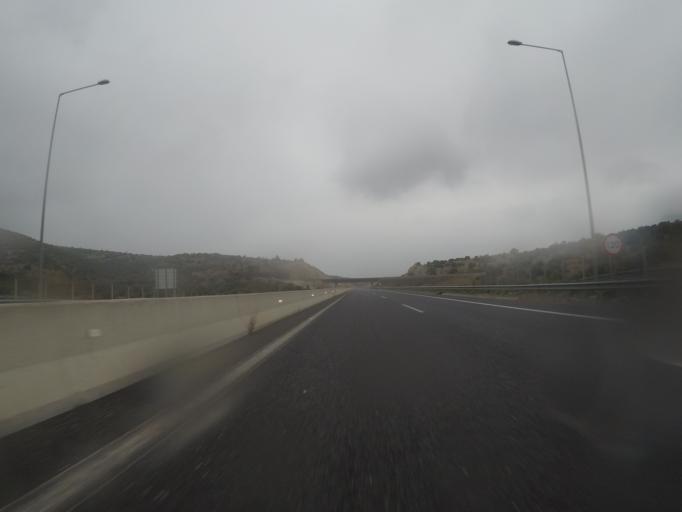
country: GR
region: Peloponnese
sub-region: Nomos Arkadias
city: Tripoli
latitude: 37.4087
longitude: 22.3060
